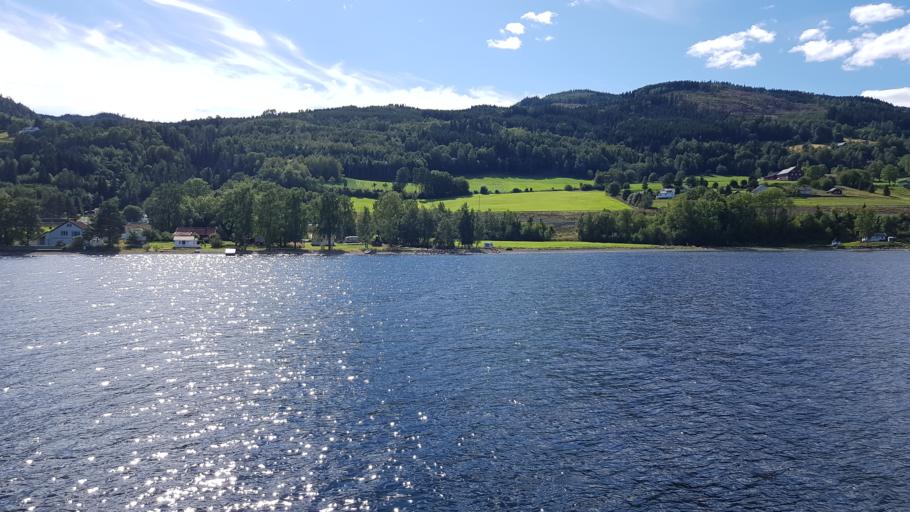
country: NO
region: Hedmark
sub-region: Stange
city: Stange
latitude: 60.6340
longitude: 11.0907
